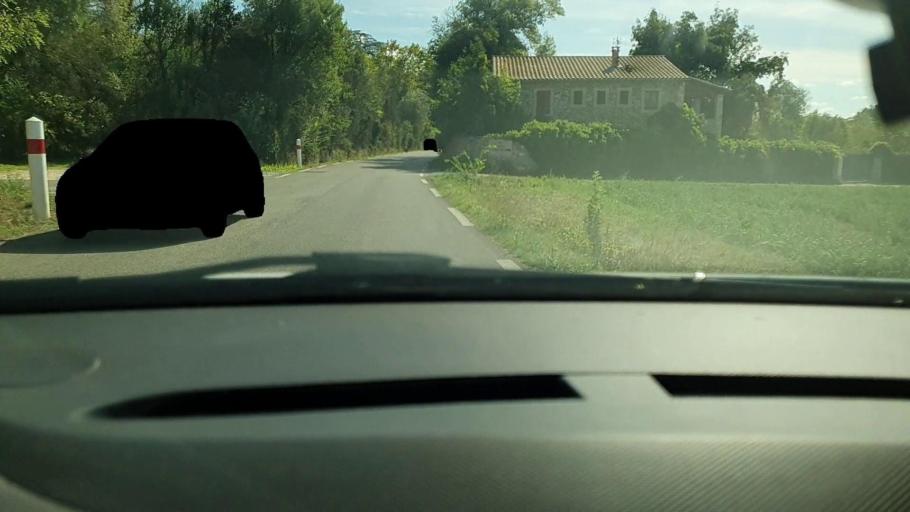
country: FR
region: Languedoc-Roussillon
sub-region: Departement du Gard
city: Saint-Ambroix
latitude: 44.2455
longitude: 4.2178
